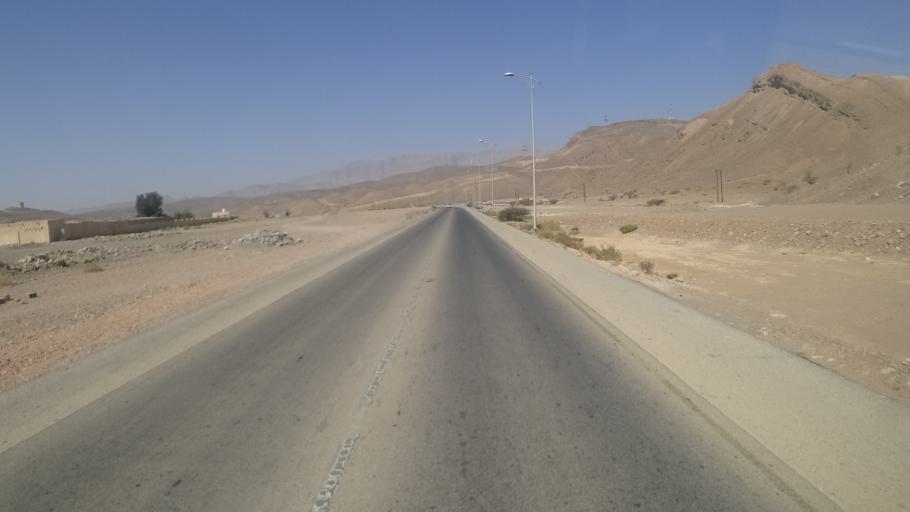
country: OM
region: Ash Sharqiyah
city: Sur
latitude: 22.5062
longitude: 59.4128
